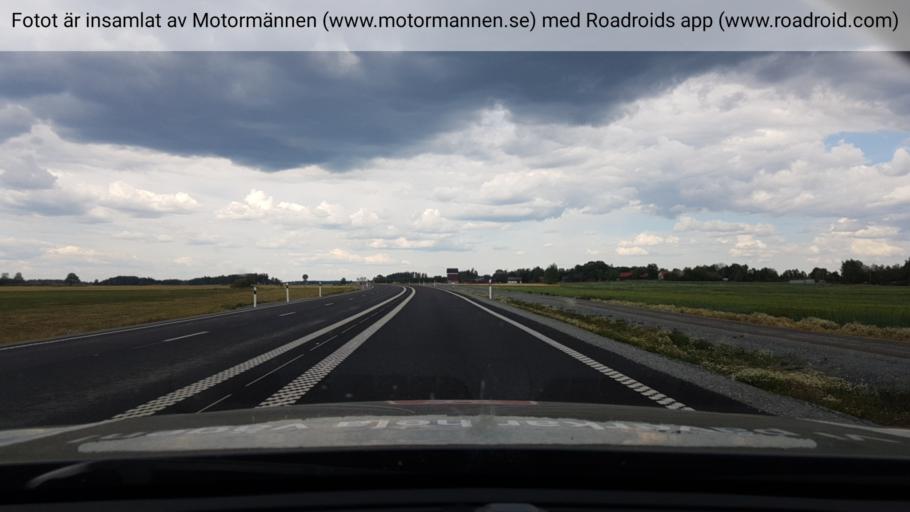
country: SE
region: Uppsala
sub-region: Enkopings Kommun
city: Irsta
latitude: 59.7456
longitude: 16.9487
